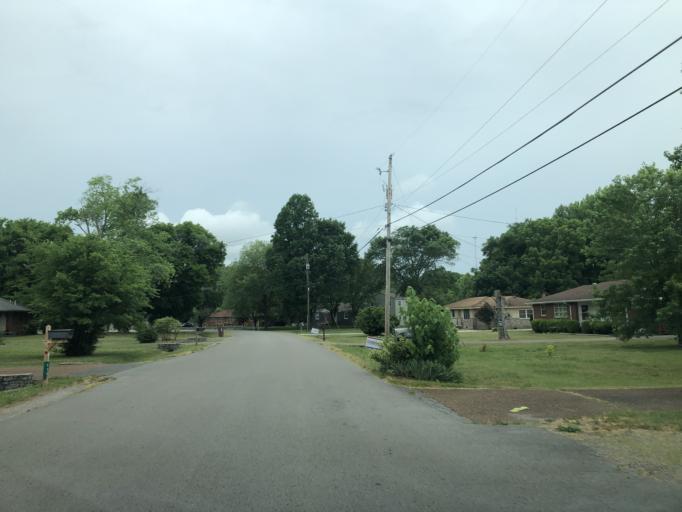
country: US
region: Tennessee
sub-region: Davidson County
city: Goodlettsville
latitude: 36.2613
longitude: -86.7614
